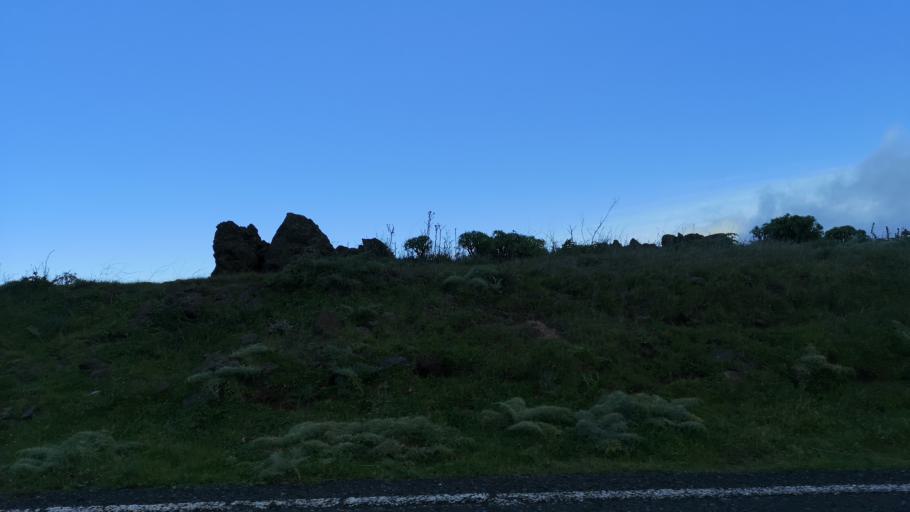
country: ES
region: Canary Islands
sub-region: Provincia de Santa Cruz de Tenerife
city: Alajero
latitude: 28.0887
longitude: -17.2557
